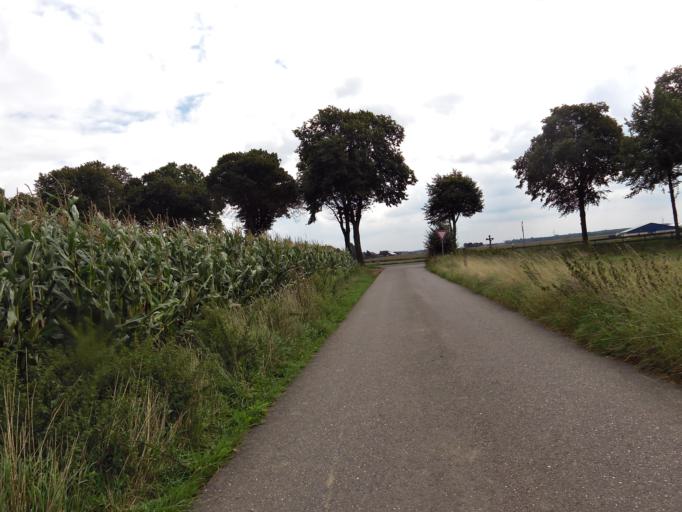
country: DE
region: North Rhine-Westphalia
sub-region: Regierungsbezirk Koln
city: Heinsberg
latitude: 51.0118
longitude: 6.0646
